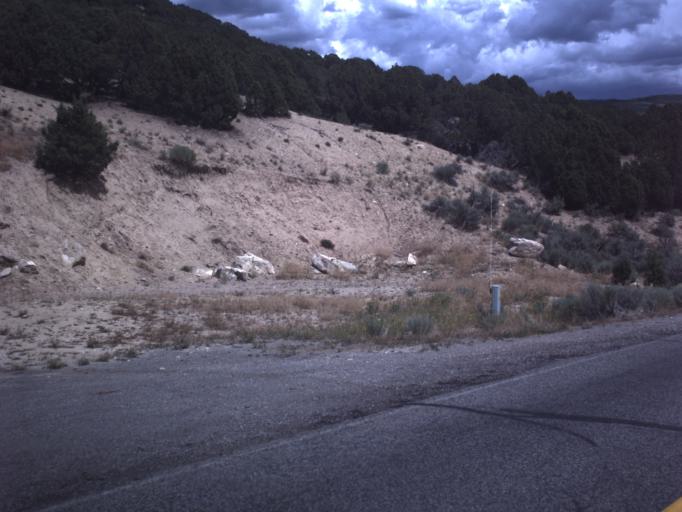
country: US
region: Utah
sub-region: Summit County
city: Oakley
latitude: 40.7635
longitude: -111.3809
